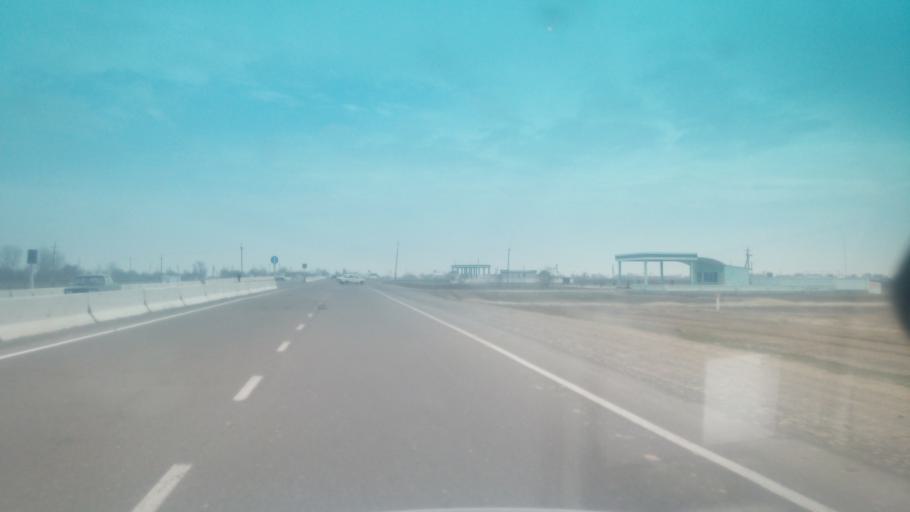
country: KZ
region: Ongtustik Qazaqstan
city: Myrzakent
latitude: 40.5050
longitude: 68.5169
